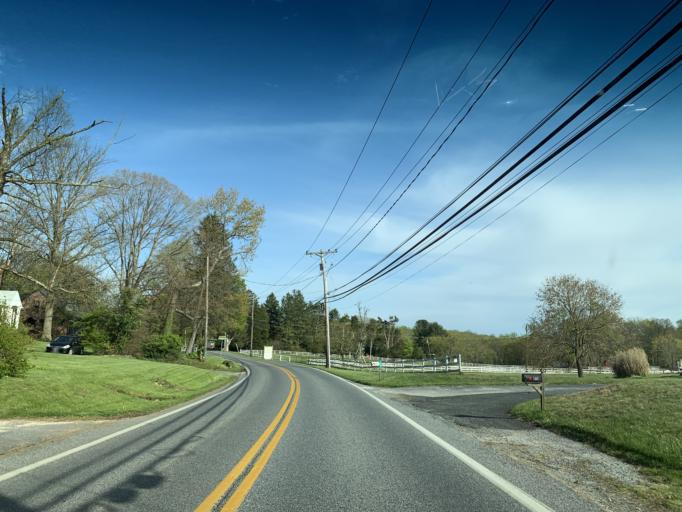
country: US
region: Maryland
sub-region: Baltimore County
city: Kingsville
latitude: 39.4416
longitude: -76.4118
